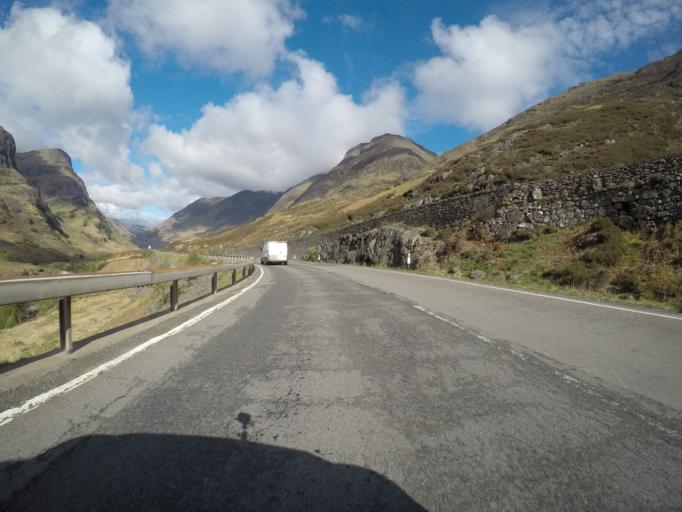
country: GB
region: Scotland
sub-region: Highland
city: Fort William
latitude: 56.6647
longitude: -4.9713
